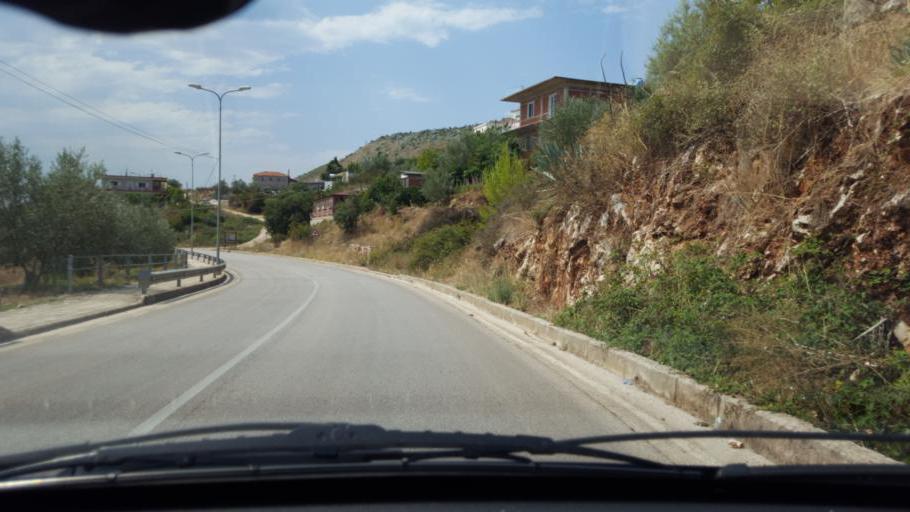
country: AL
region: Vlore
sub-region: Rrethi i Sarandes
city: Sarande
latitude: 39.8393
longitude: 20.0236
